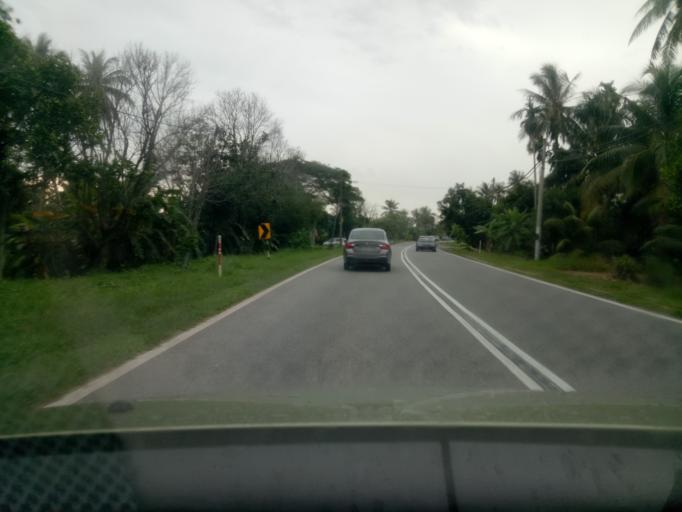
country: MY
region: Kedah
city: Gurun
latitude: 5.9688
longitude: 100.4291
